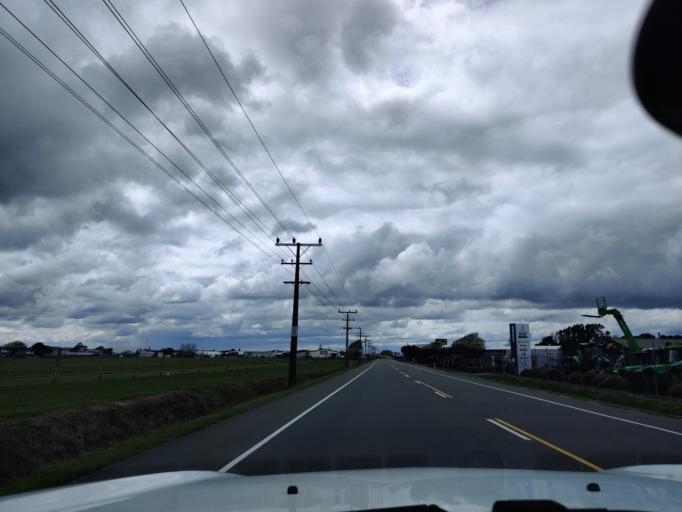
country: NZ
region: Manawatu-Wanganui
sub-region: Palmerston North City
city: Palmerston North
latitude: -40.2347
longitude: 175.5647
